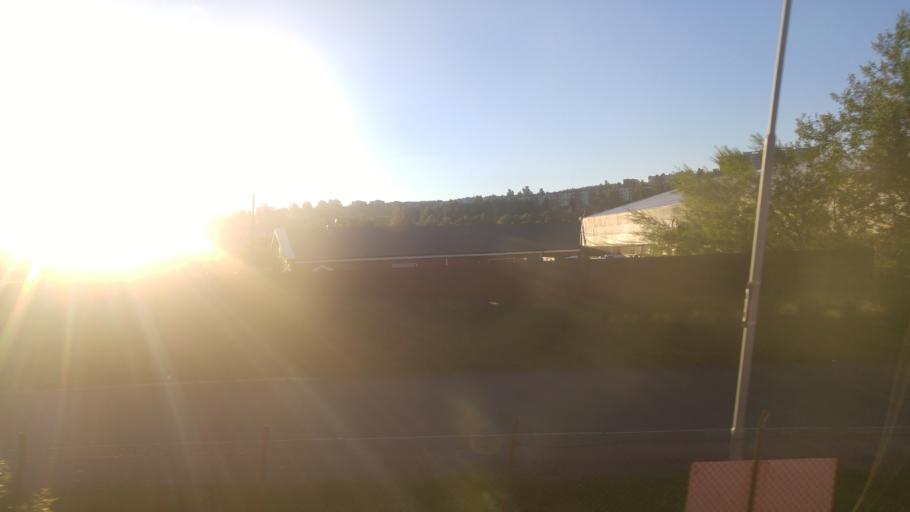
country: NO
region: Oslo
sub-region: Oslo
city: Oslo
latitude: 59.9226
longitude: 10.8331
